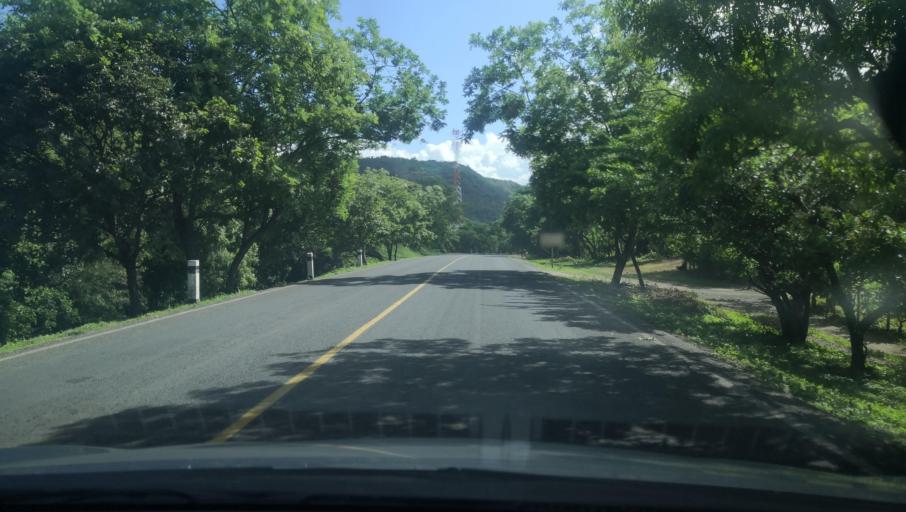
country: NI
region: Madriz
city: Somoto
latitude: 13.4703
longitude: -86.6248
